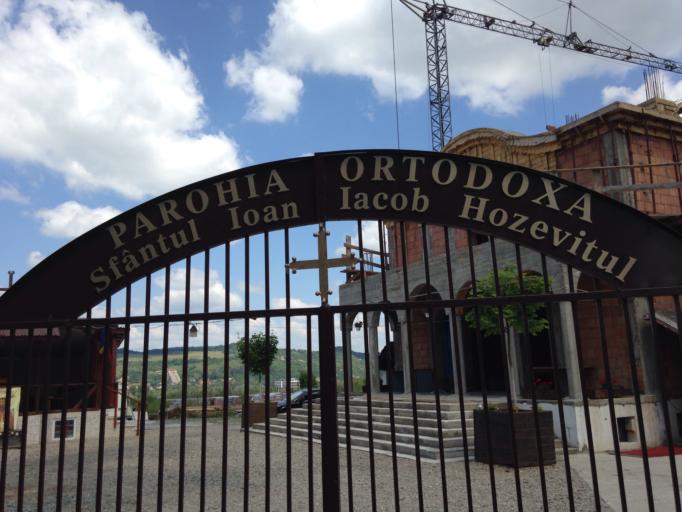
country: RO
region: Cluj
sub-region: Comuna Floresti
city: Floresti
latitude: 46.7472
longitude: 23.5322
